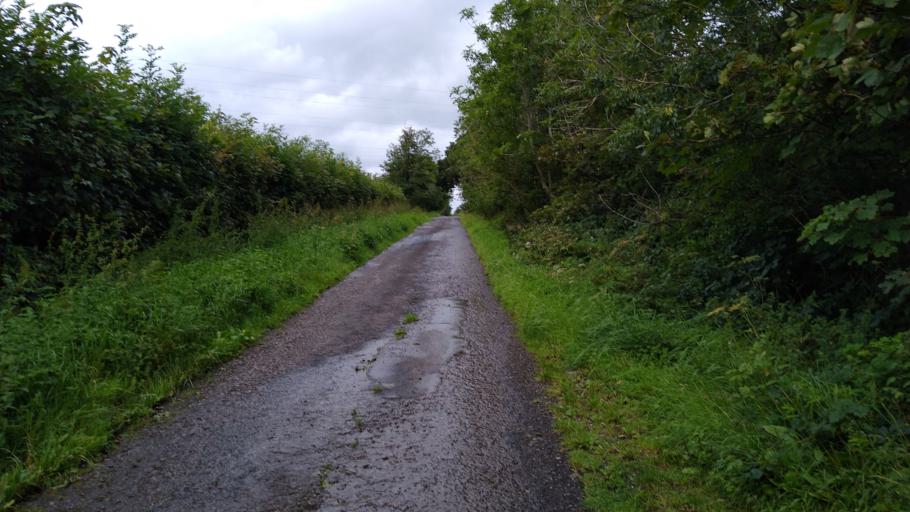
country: GB
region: England
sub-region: Cumbria
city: Cockermouth
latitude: 54.6379
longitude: -3.3393
